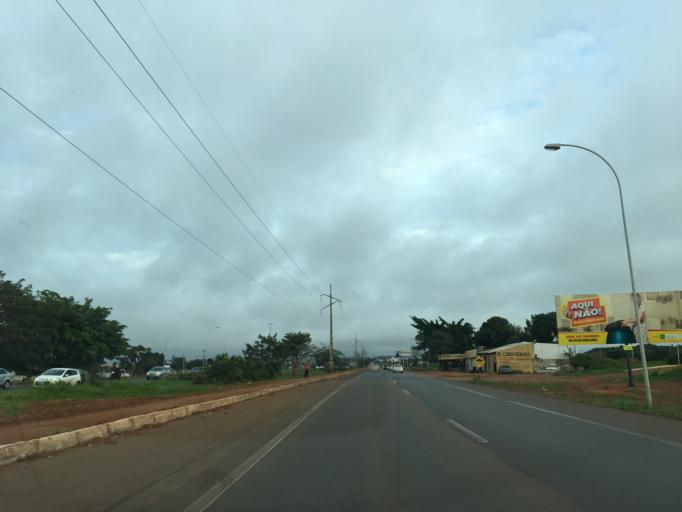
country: BR
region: Goias
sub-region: Luziania
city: Luziania
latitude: -16.0459
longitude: -48.0407
